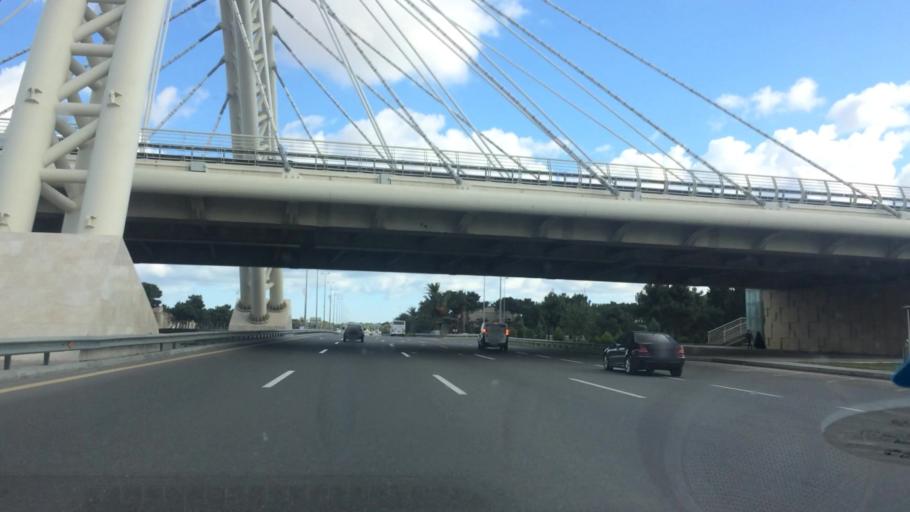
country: AZ
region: Baki
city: Biny Selo
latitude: 40.4590
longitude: 50.0753
